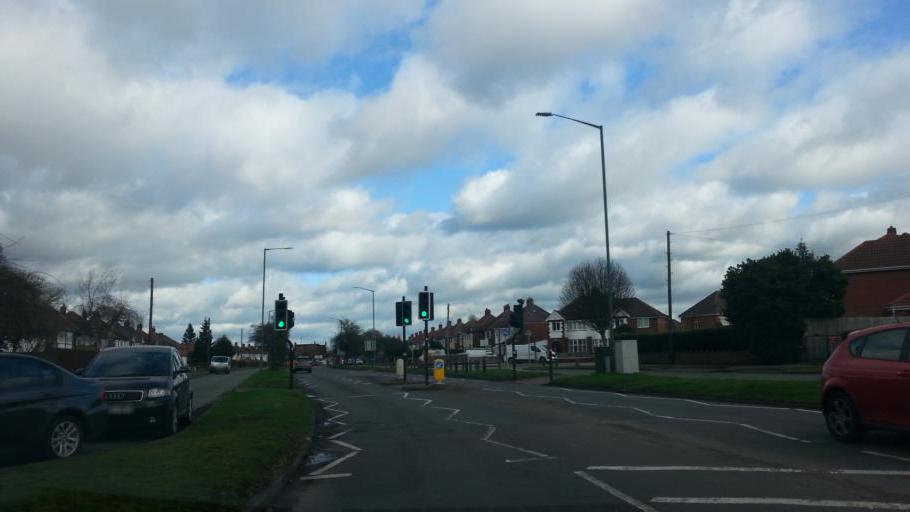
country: GB
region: England
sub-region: City and Borough of Birmingham
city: Acocks Green
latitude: 52.4479
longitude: -1.7840
